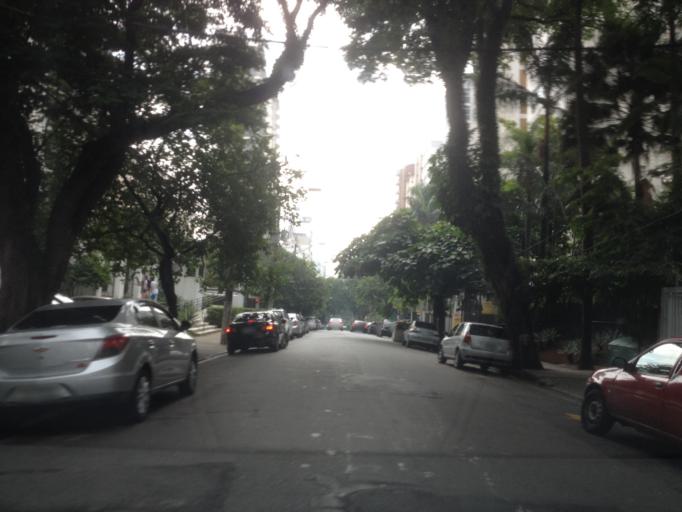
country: BR
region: Sao Paulo
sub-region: Sao Paulo
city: Sao Paulo
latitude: -23.5813
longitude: -46.6718
